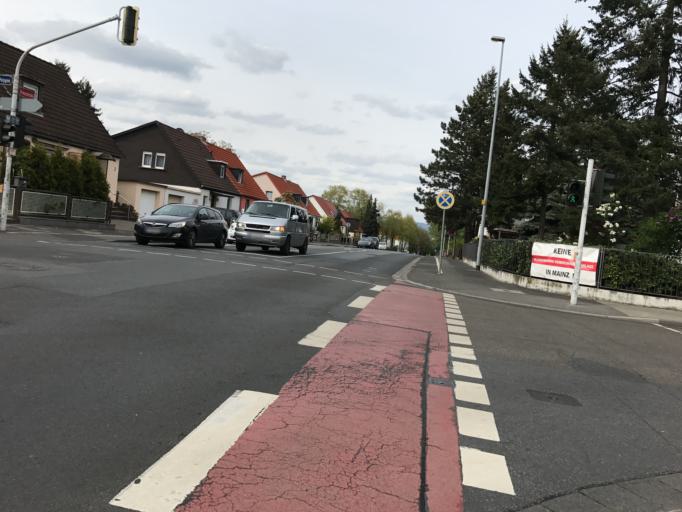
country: DE
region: Rheinland-Pfalz
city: Budenheim
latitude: 50.0158
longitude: 8.2193
